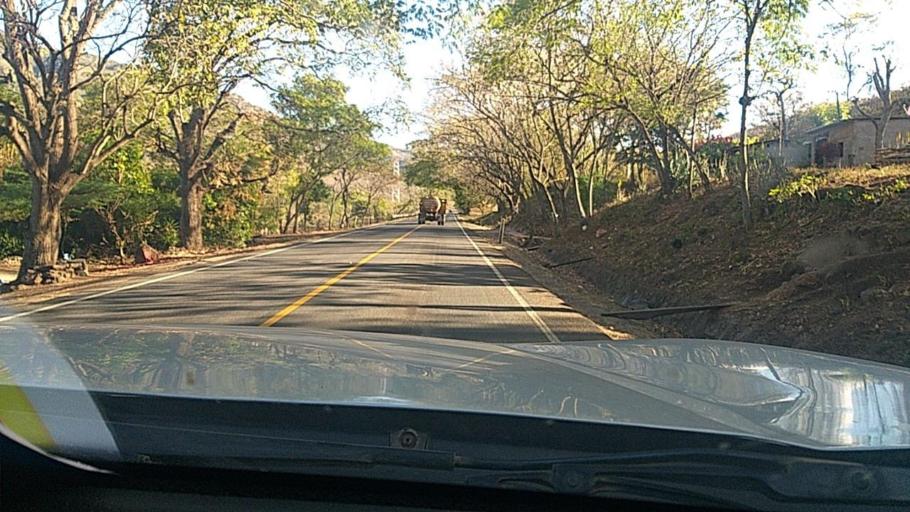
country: NI
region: Esteli
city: Condega
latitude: 13.2892
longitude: -86.3465
